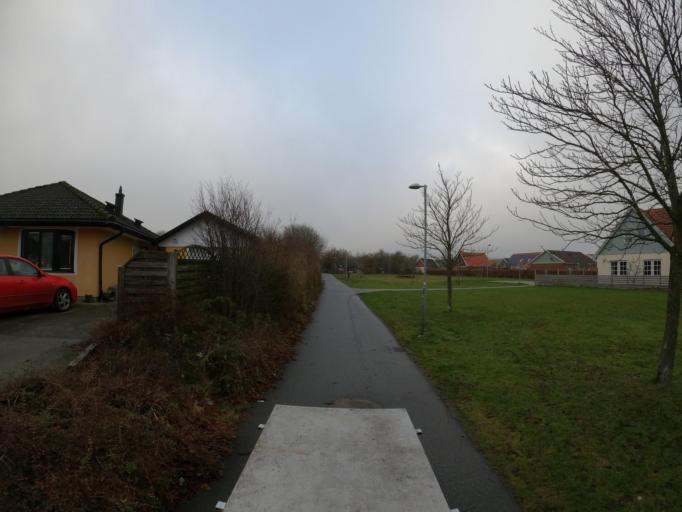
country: SE
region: Skane
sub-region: Svedala Kommun
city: Svedala
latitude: 55.5177
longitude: 13.2354
